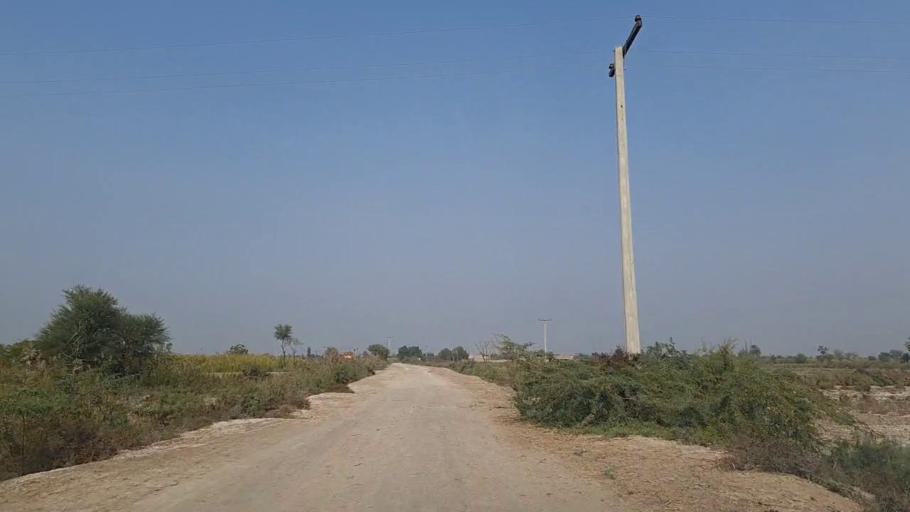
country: PK
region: Sindh
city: Daur
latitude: 26.4851
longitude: 68.4514
